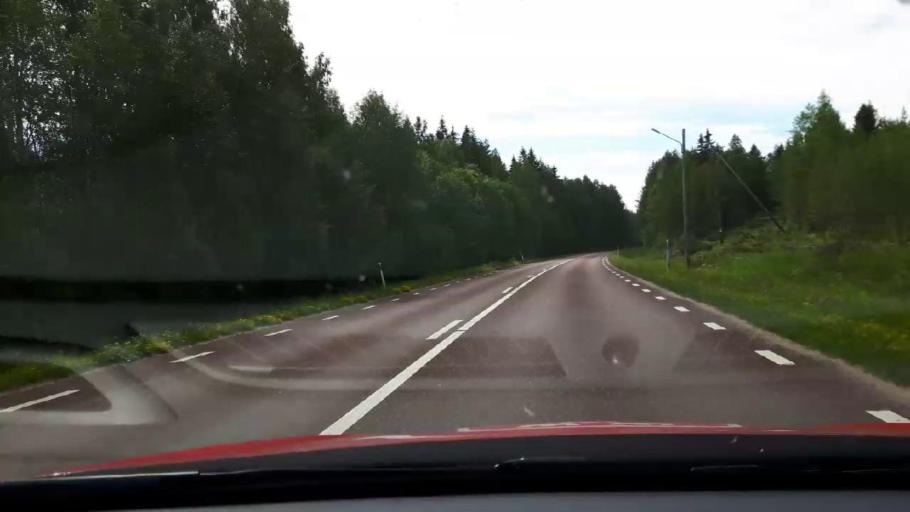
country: SE
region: Jaemtland
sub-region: Harjedalens Kommun
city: Sveg
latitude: 62.0727
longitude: 14.9403
